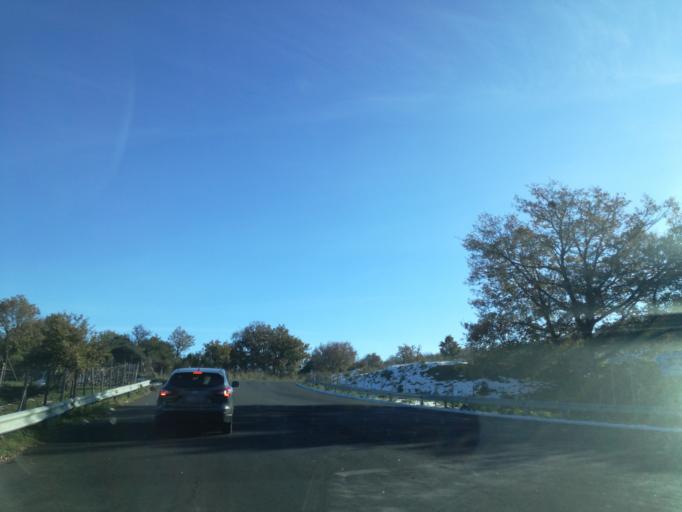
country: IT
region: Sicily
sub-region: Catania
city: Randazzo
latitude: 37.8561
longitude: 14.9848
